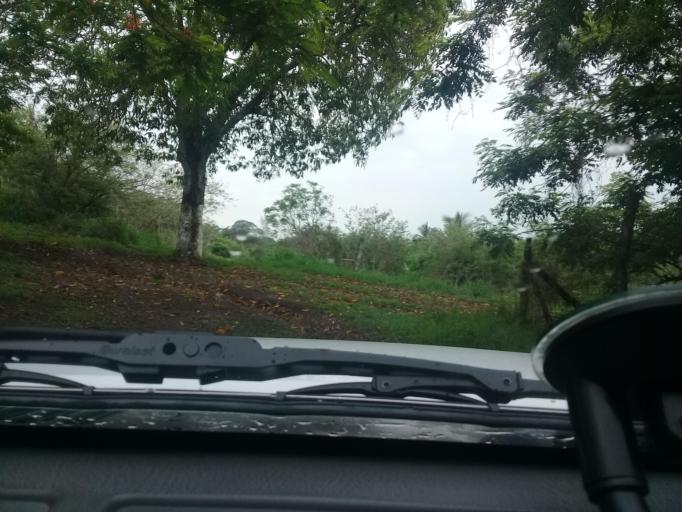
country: MX
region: Veracruz
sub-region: Puente Nacional
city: Cabezas
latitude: 19.3661
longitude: -96.3986
